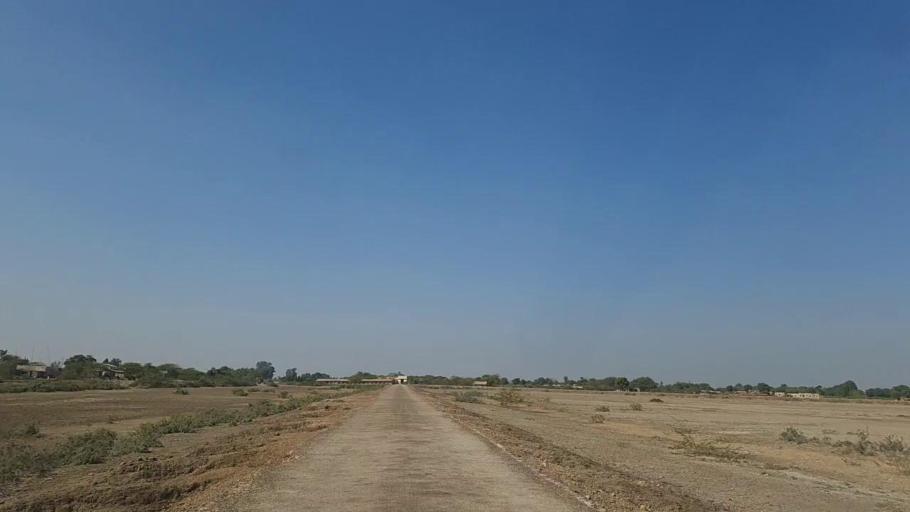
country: PK
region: Sindh
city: Samaro
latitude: 25.3966
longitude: 69.4014
